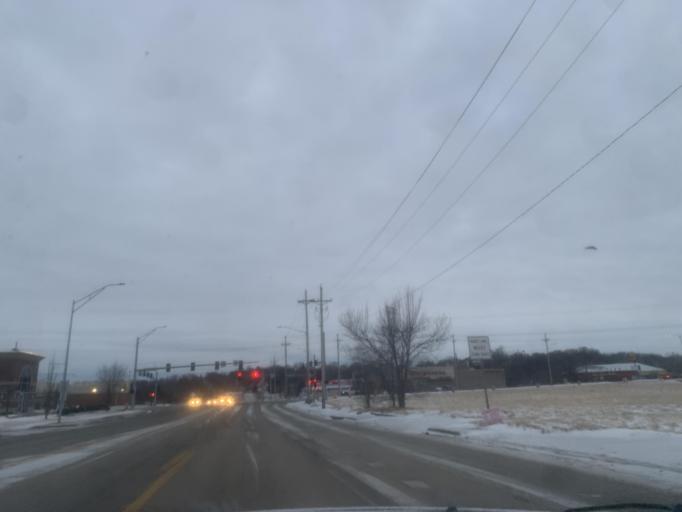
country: US
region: Nebraska
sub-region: Douglas County
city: Ralston
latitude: 41.2353
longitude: -96.0526
